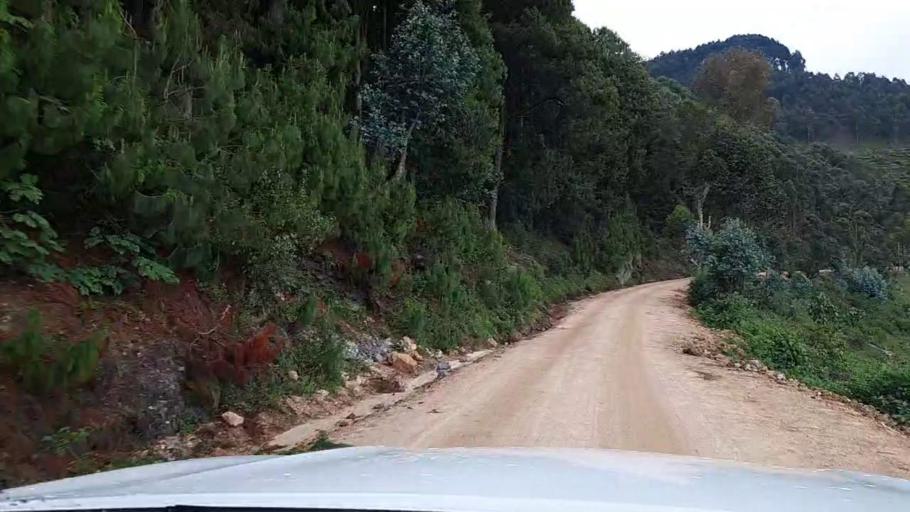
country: RW
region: Western Province
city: Kibuye
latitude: -2.3001
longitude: 29.3827
